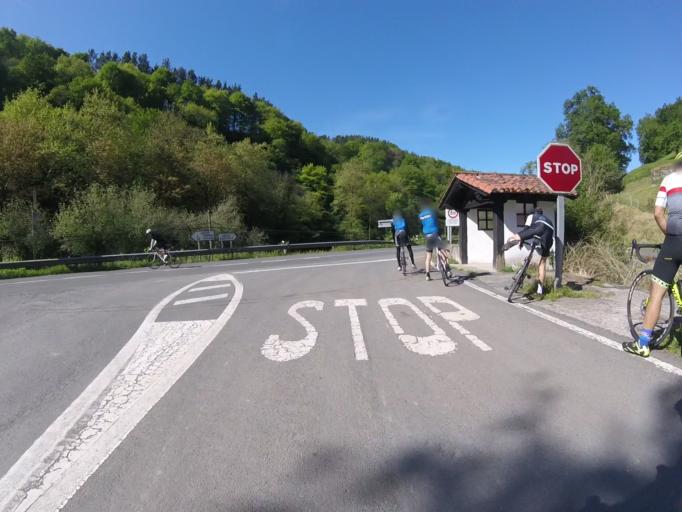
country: ES
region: Basque Country
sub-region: Provincia de Guipuzcoa
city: Errezil
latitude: 43.1744
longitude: -2.2057
